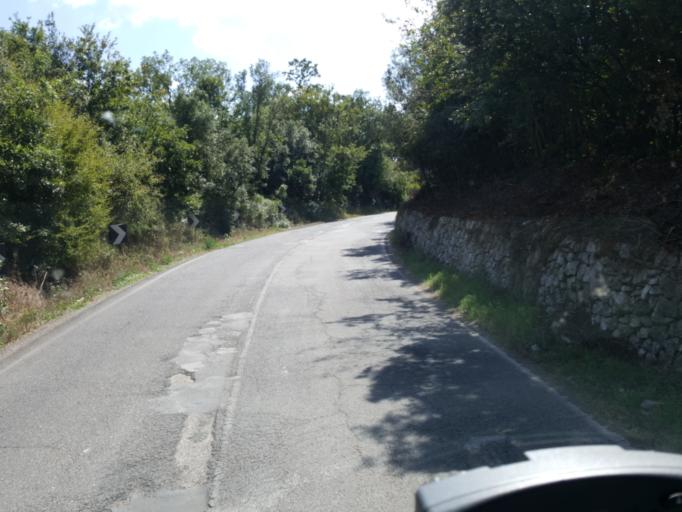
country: IT
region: Latium
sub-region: Provincia di Latina
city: Priverno
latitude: 41.4446
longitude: 13.2022
